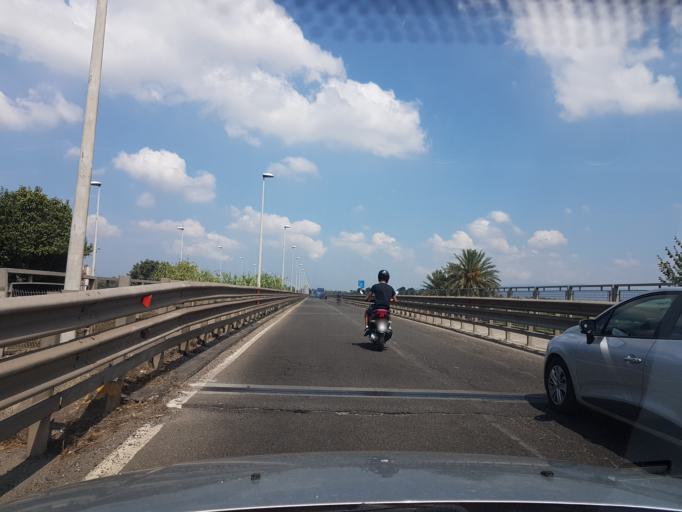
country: IT
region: Sardinia
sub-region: Provincia di Oristano
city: Oristano
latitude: 39.9171
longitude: 8.5842
